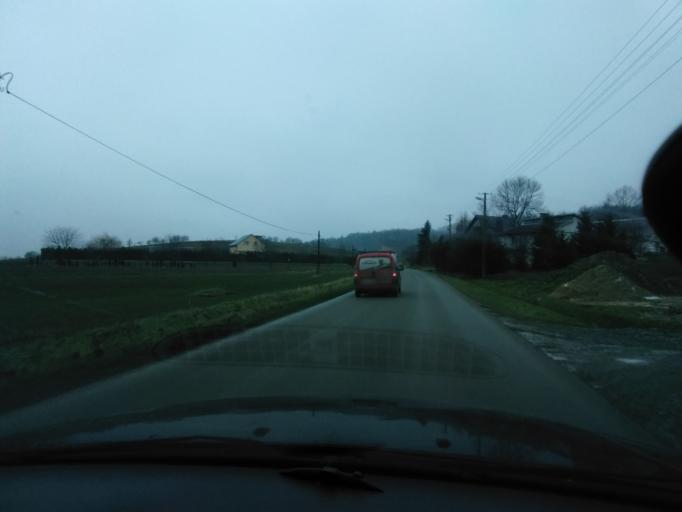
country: PL
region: Subcarpathian Voivodeship
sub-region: Powiat przeworski
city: Zarzecze
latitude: 49.9926
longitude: 22.5217
